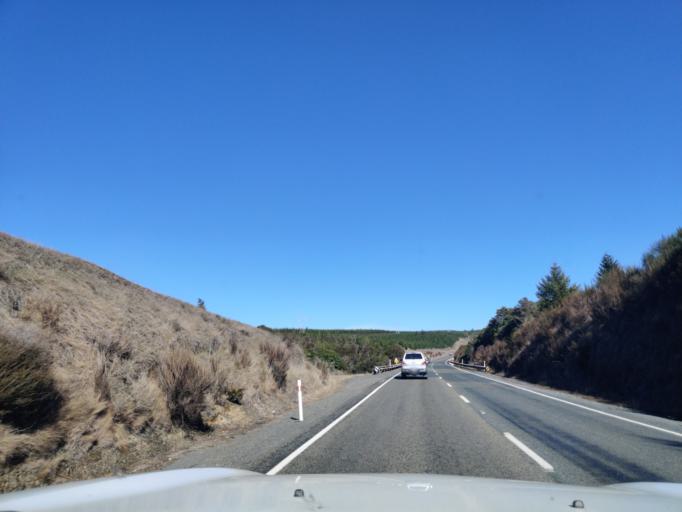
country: NZ
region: Waikato
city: Turangi
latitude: -39.1088
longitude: 175.8071
